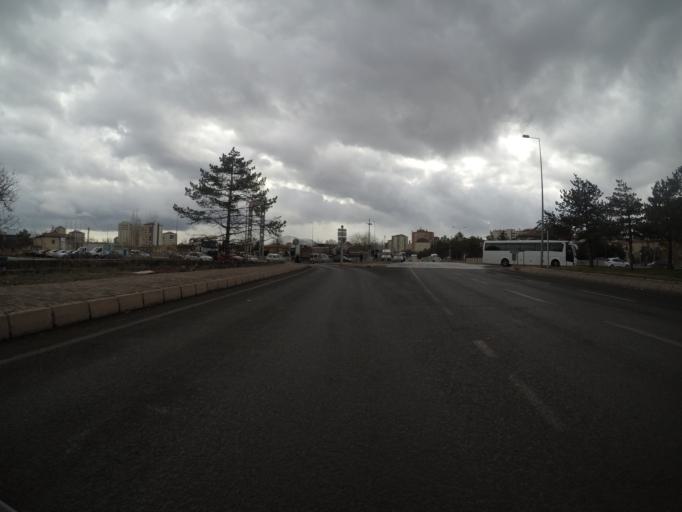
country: TR
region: Kayseri
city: Melikgazi
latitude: 38.7506
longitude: 35.4711
